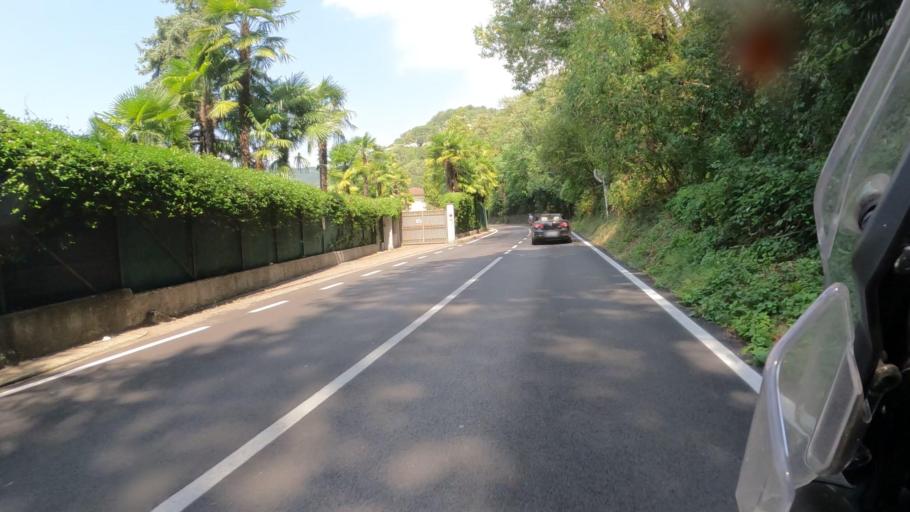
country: IT
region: Lombardy
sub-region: Provincia di Varese
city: Luino
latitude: 46.0079
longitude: 8.7473
